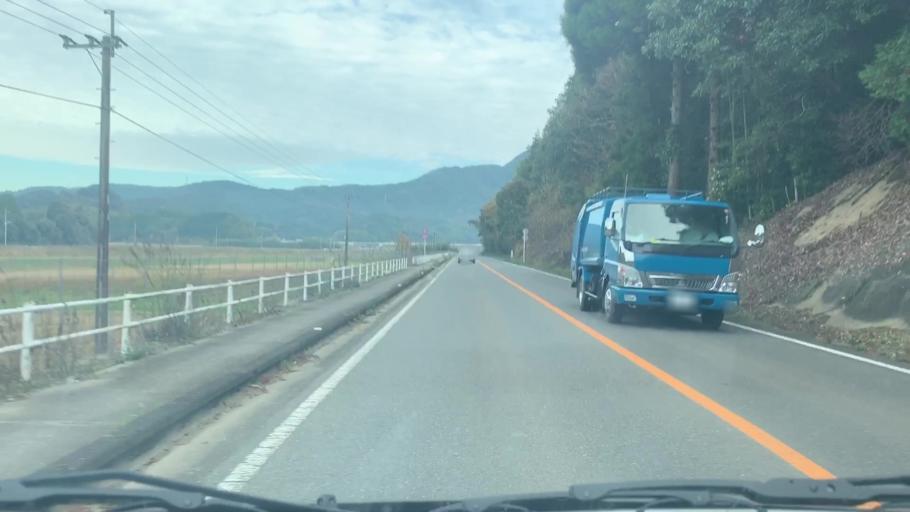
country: JP
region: Saga Prefecture
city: Takeocho-takeo
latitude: 33.2513
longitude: 129.9696
